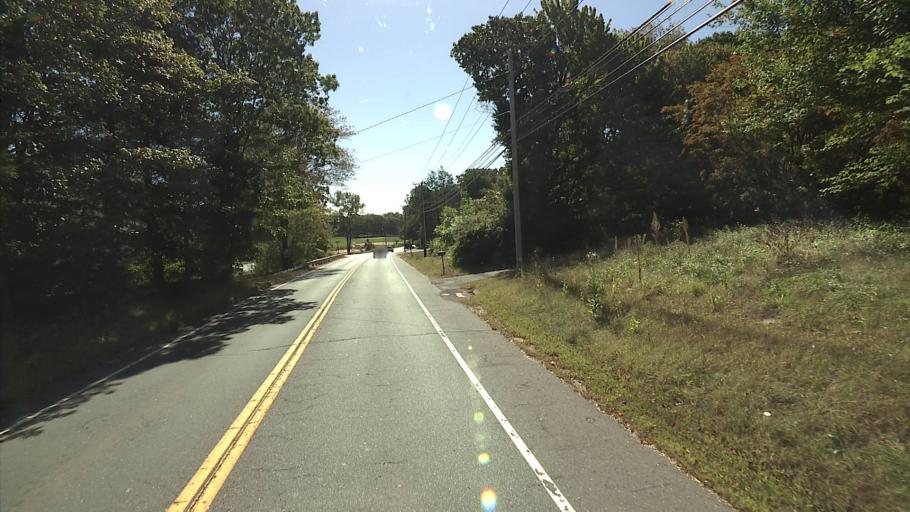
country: US
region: Connecticut
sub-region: New Haven County
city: Prospect
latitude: 41.4992
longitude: -72.9778
